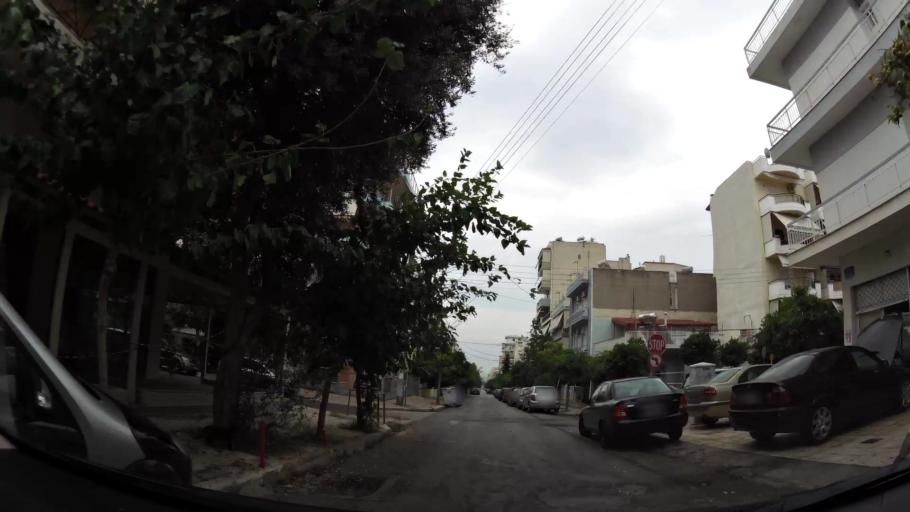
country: GR
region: Attica
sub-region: Nomarchia Athinas
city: Agia Varvara
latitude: 37.9803
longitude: 23.6579
